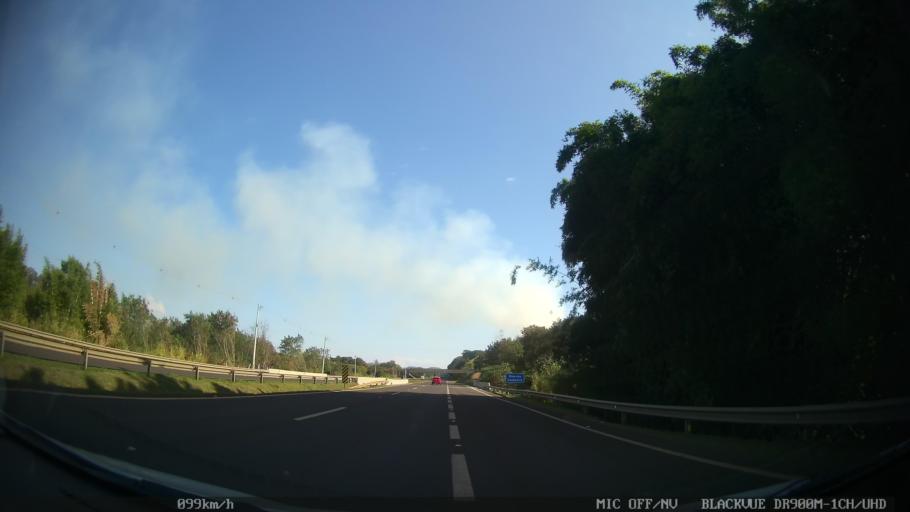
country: BR
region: Sao Paulo
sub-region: Piracicaba
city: Piracicaba
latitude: -22.6850
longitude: -47.5809
